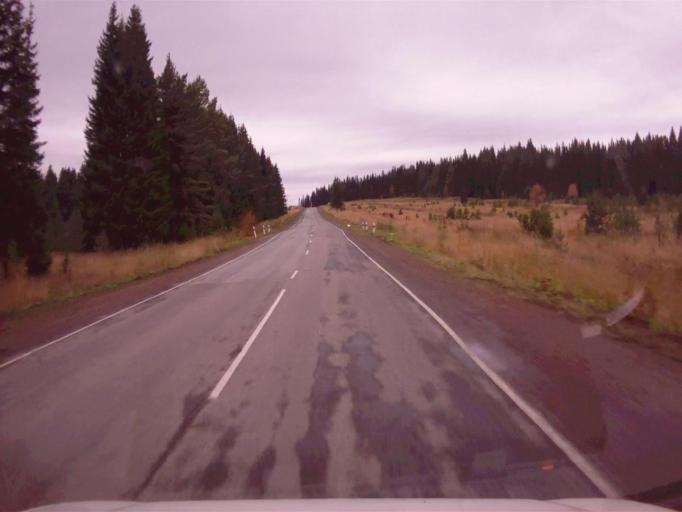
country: RU
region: Chelyabinsk
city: Nyazepetrovsk
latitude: 56.0664
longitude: 59.6438
